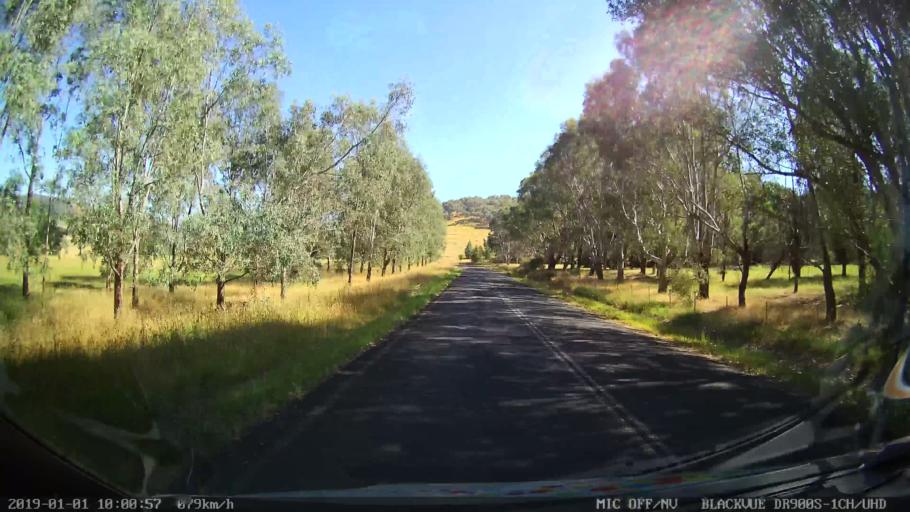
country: AU
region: New South Wales
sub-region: Snowy River
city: Jindabyne
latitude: -36.1966
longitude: 148.1029
